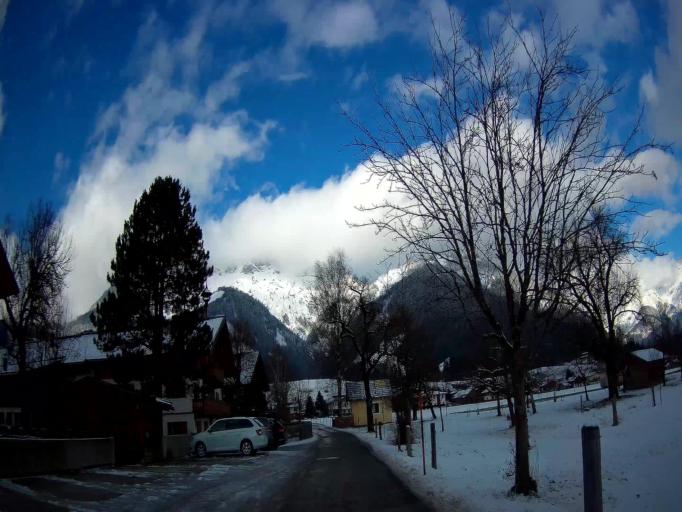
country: AT
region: Salzburg
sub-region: Politischer Bezirk Zell am See
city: Leogang
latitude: 47.4424
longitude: 12.7963
